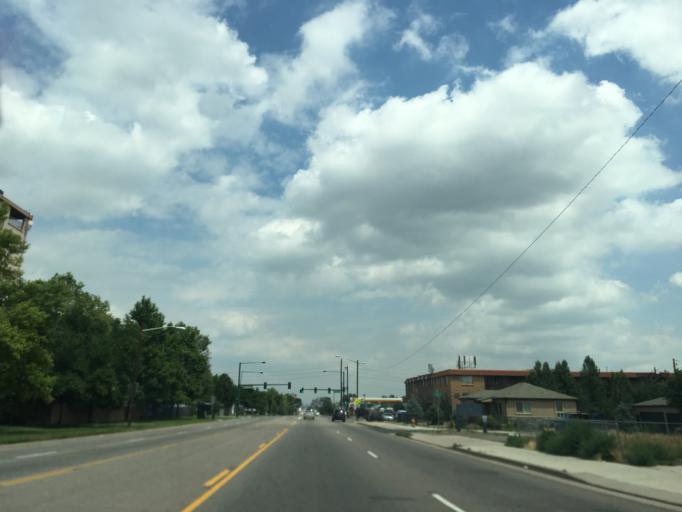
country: US
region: Colorado
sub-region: Arapahoe County
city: Sheridan
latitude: 39.6662
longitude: -105.0251
